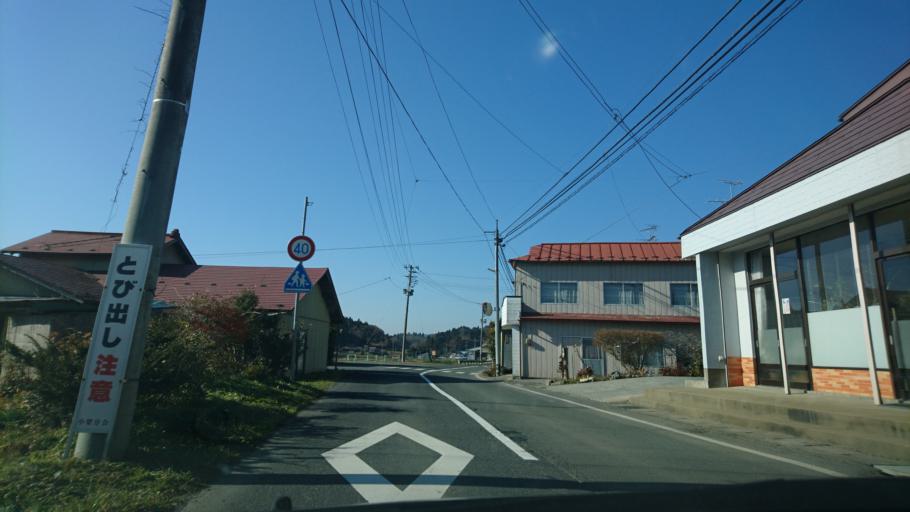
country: JP
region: Iwate
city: Ichinoseki
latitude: 38.9013
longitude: 141.3835
